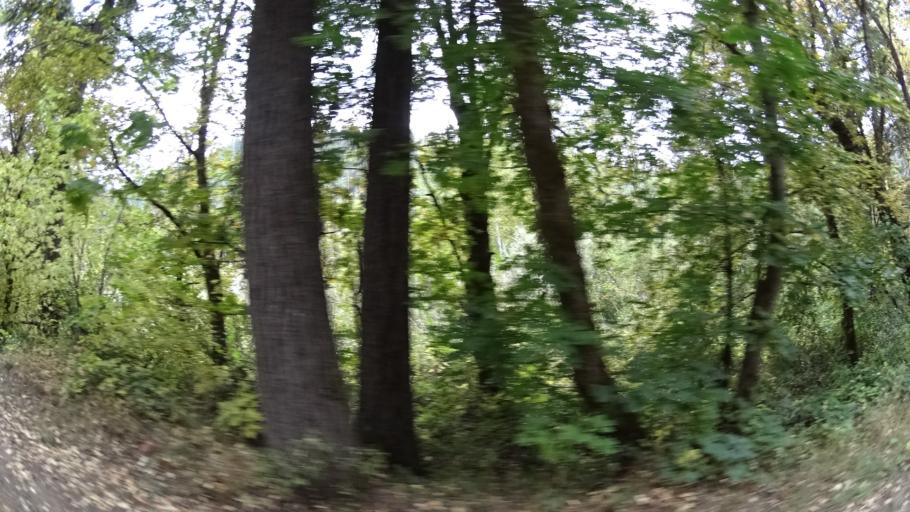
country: US
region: California
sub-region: Siskiyou County
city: Happy Camp
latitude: 41.7774
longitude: -123.3285
